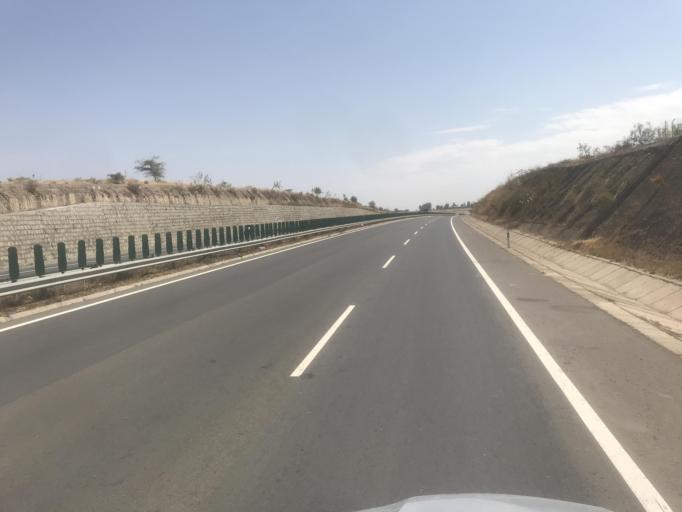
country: ET
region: Oromiya
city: Mojo
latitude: 8.5838
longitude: 39.1670
